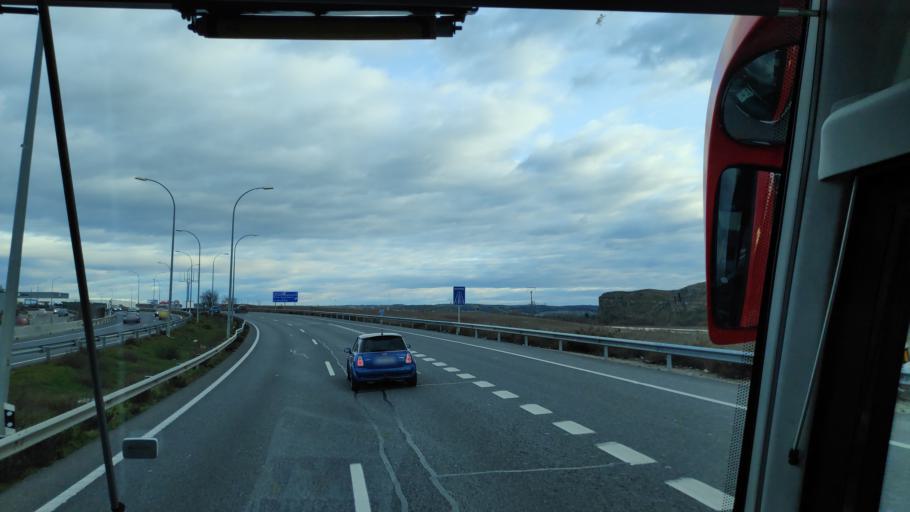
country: ES
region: Madrid
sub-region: Provincia de Madrid
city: Vaciamadrid
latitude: 40.3358
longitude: -3.5352
